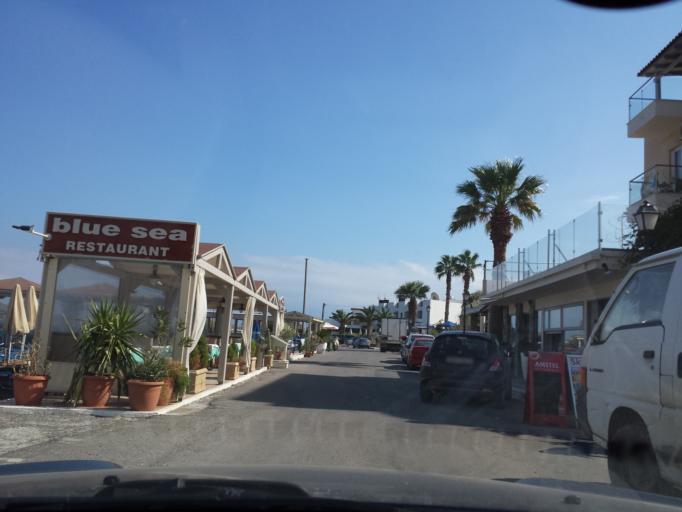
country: GR
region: Crete
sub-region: Nomos Lasithiou
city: Skhisma
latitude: 35.2592
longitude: 25.7282
